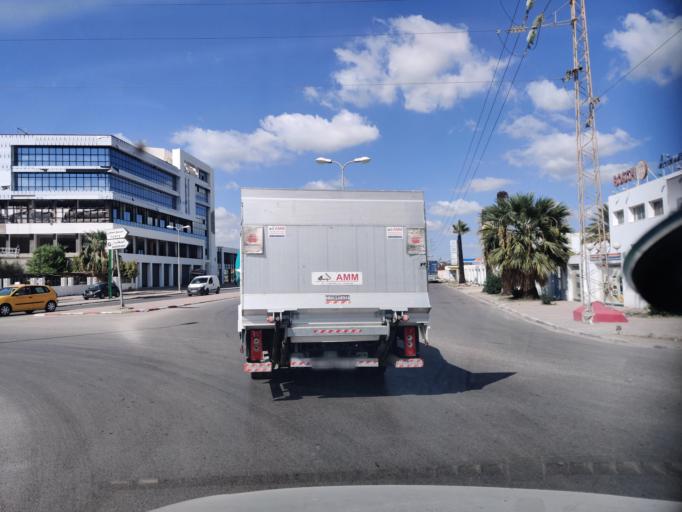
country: TN
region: Bin 'Arus
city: Ben Arous
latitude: 36.7755
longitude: 10.2149
